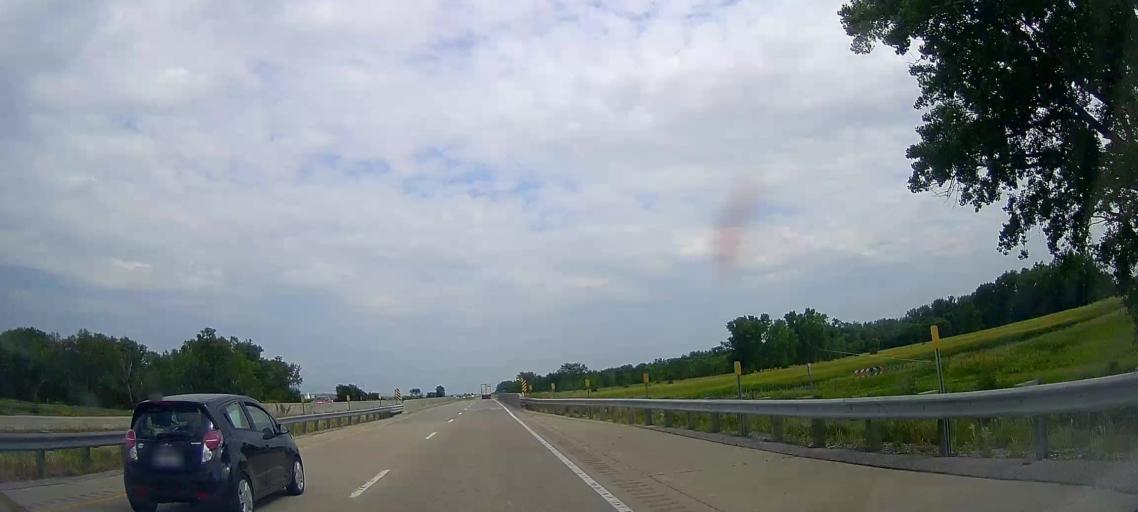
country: US
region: Nebraska
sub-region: Burt County
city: Tekamah
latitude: 41.8212
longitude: -96.0732
